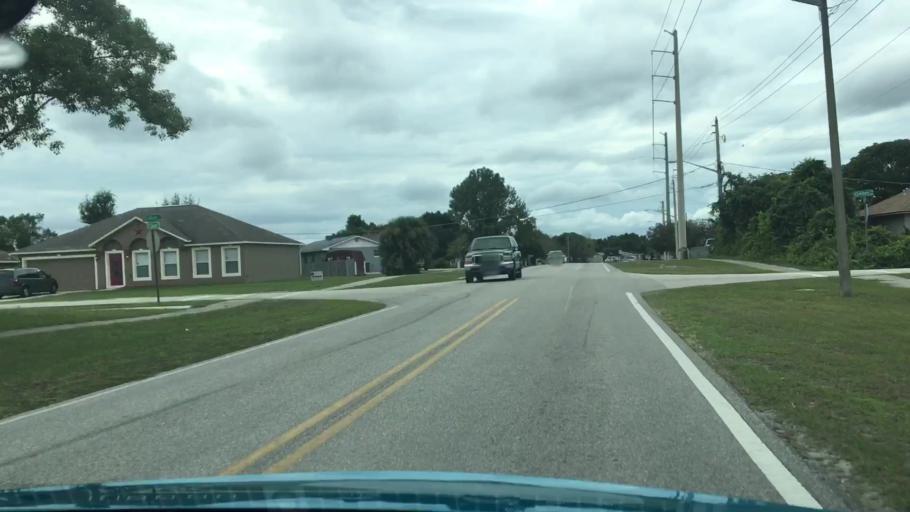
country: US
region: Florida
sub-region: Volusia County
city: Lake Helen
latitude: 28.9324
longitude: -81.1797
